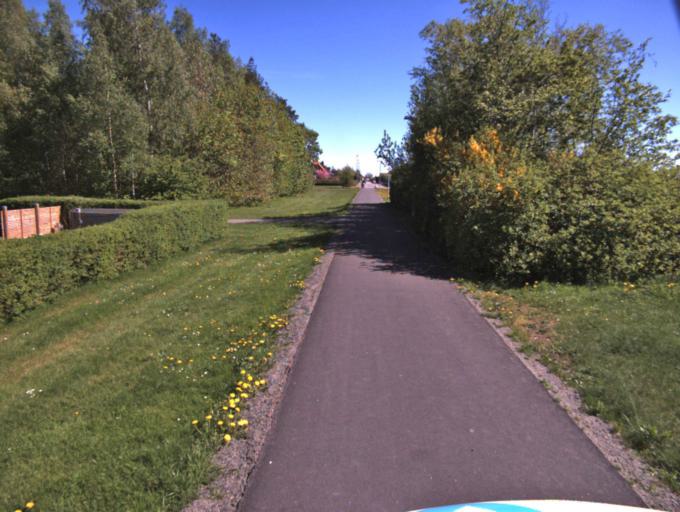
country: SE
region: Skane
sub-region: Kristianstads Kommun
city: Norra Asum
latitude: 56.0012
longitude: 14.1431
